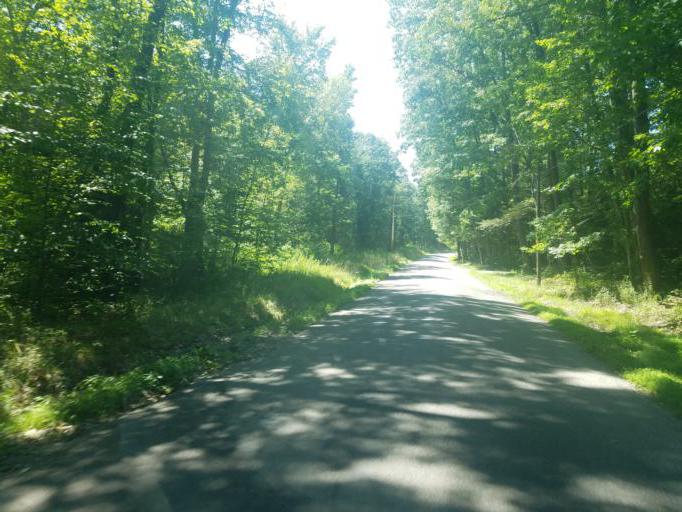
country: US
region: Pennsylvania
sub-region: Clarion County
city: Knox
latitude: 41.1969
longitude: -79.5218
